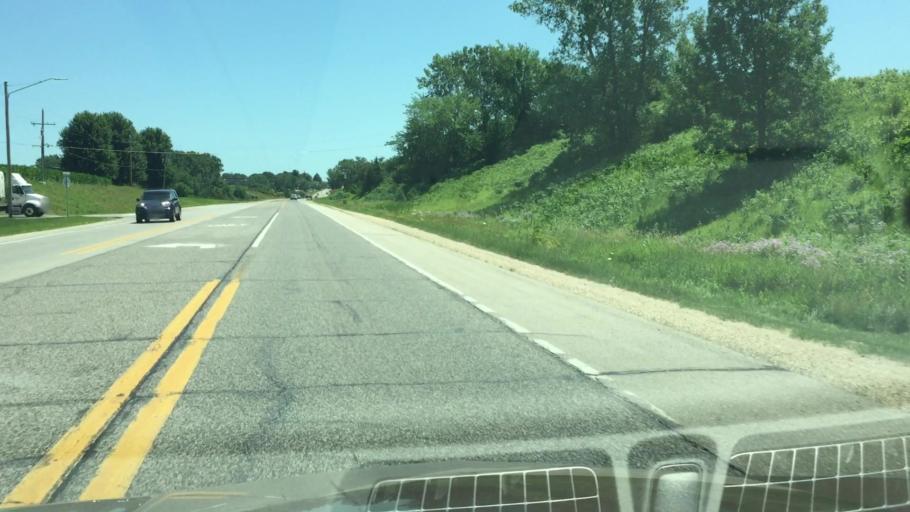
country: US
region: Iowa
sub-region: Linn County
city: Lisbon
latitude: 41.9173
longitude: -91.4011
